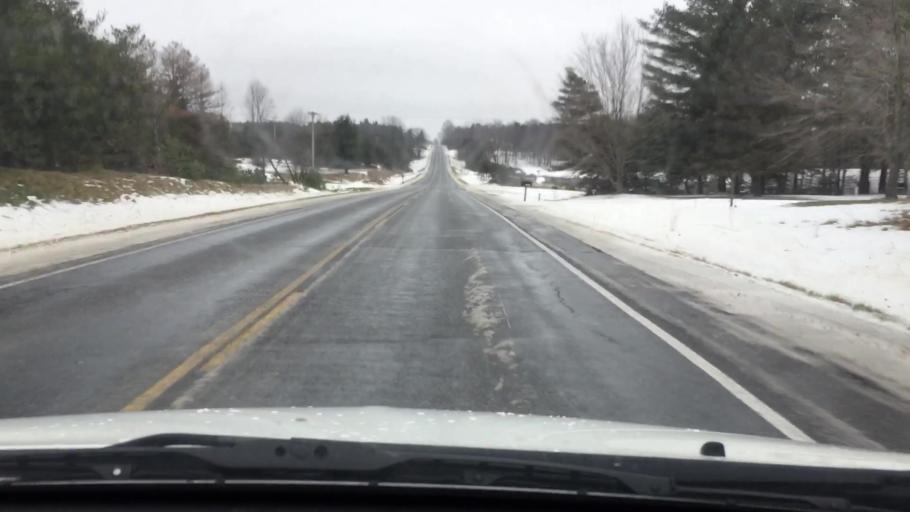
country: US
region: Michigan
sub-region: Wexford County
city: Cadillac
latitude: 44.0892
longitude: -85.4441
